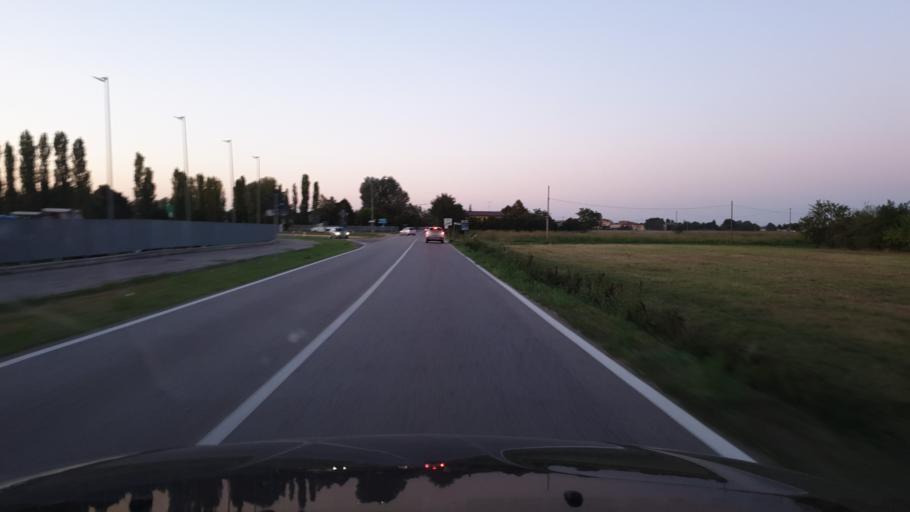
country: IT
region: Emilia-Romagna
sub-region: Provincia di Bologna
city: Altedo
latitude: 44.6813
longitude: 11.4968
